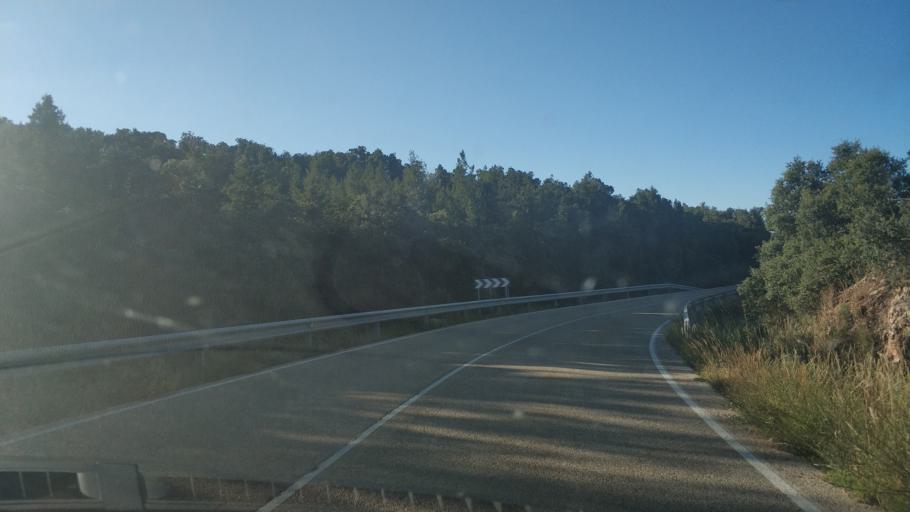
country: ES
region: Castille and Leon
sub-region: Provincia de Soria
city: Montejo de Tiermes
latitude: 41.4196
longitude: -3.2052
